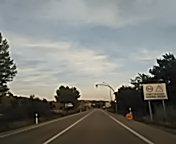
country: ES
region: Castille and Leon
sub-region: Provincia de Soria
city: San Leonardo de Yague
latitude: 41.8338
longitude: -3.0761
